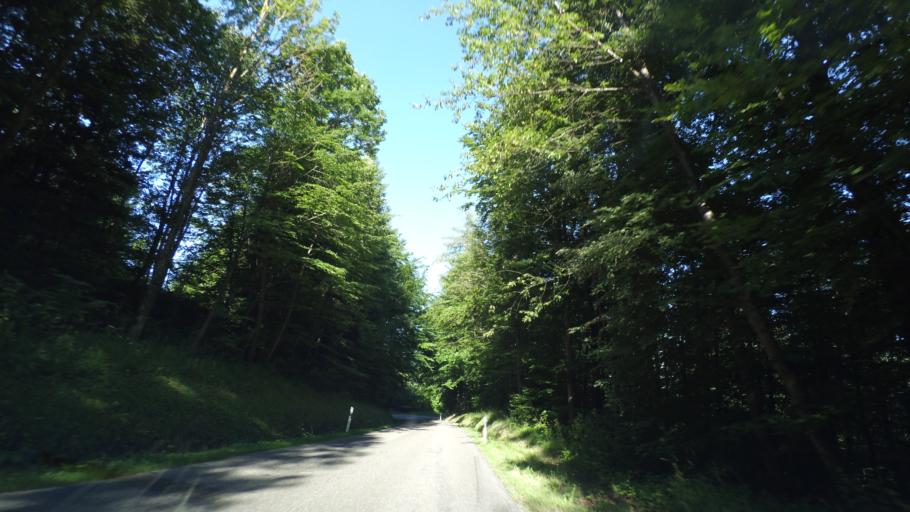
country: DE
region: Baden-Wuerttemberg
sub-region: Regierungsbezirk Stuttgart
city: Murrhardt
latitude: 48.9869
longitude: 9.6044
